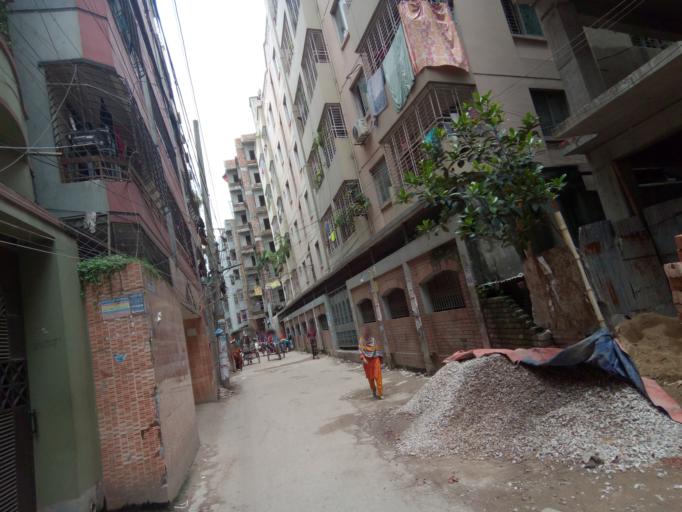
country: BD
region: Dhaka
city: Azimpur
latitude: 23.7661
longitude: 90.3547
